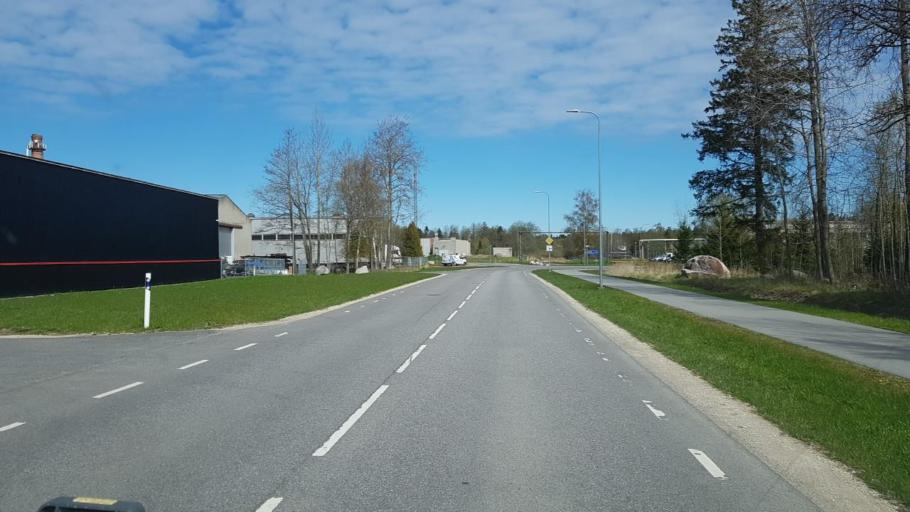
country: EE
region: Harju
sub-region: Viimsi vald
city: Rummu
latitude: 59.5409
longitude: 24.8087
